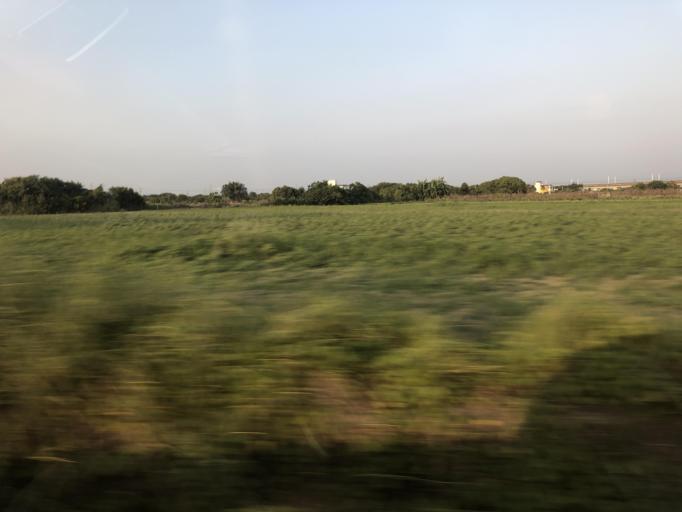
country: TW
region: Taiwan
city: Xinying
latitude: 23.1583
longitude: 120.2729
